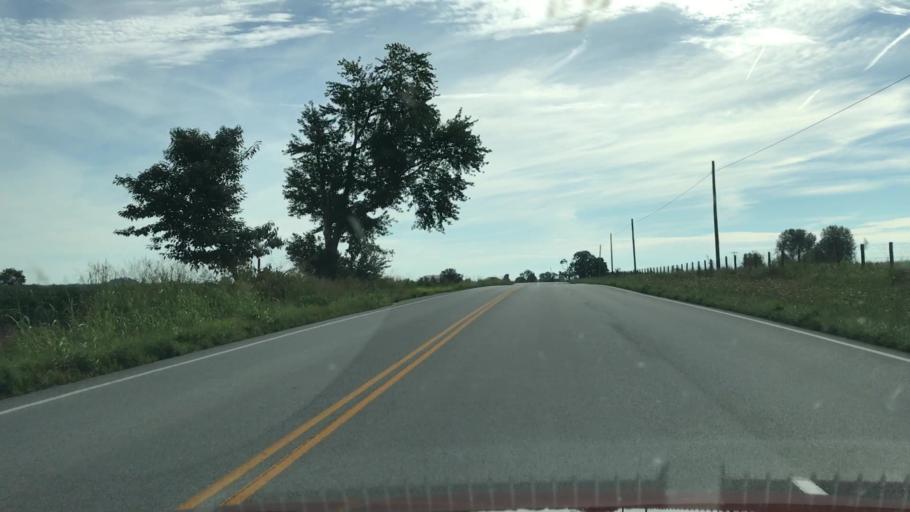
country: US
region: Kentucky
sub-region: Edmonson County
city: Brownsville
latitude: 37.0741
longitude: -86.2579
